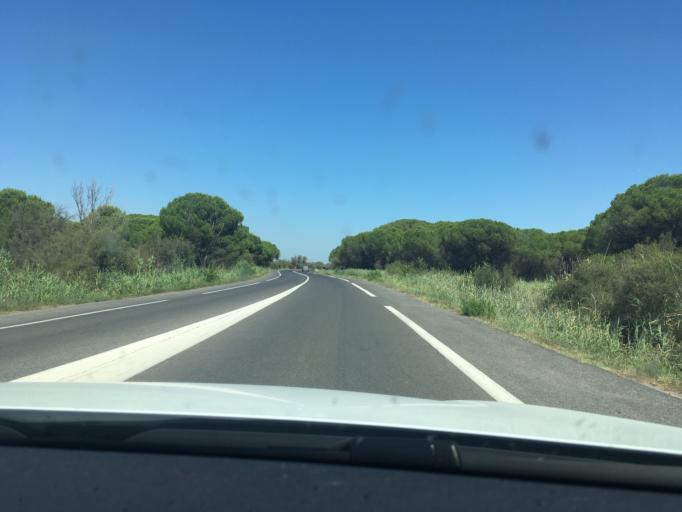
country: FR
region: Languedoc-Roussillon
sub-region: Departement du Gard
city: Le Grau-du-Roi
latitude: 43.5520
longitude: 4.1267
